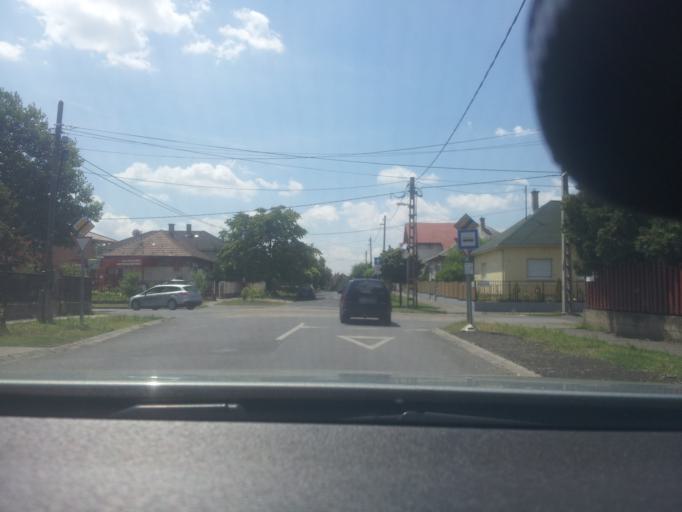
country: HU
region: Budapest
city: Budapest XVIII. keruelet
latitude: 47.4325
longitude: 19.1660
